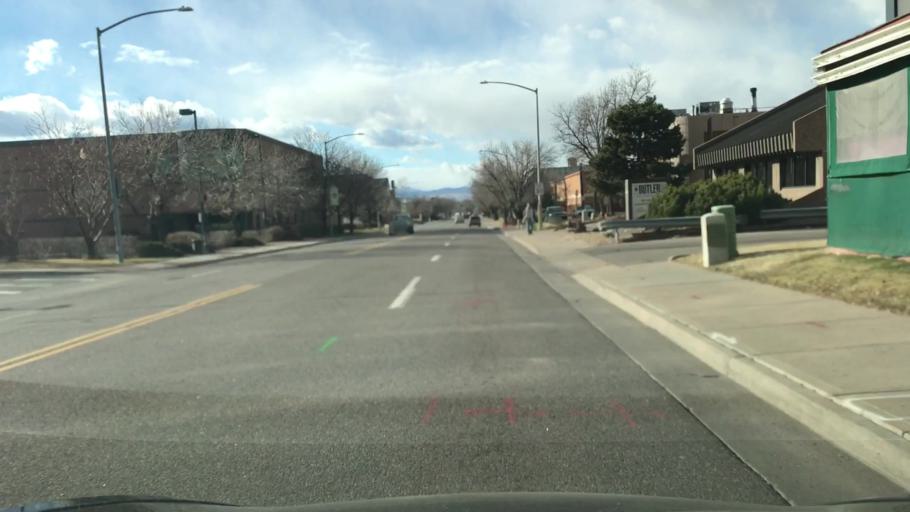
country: US
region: Colorado
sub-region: Arapahoe County
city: Glendale
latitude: 39.7074
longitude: -104.9346
